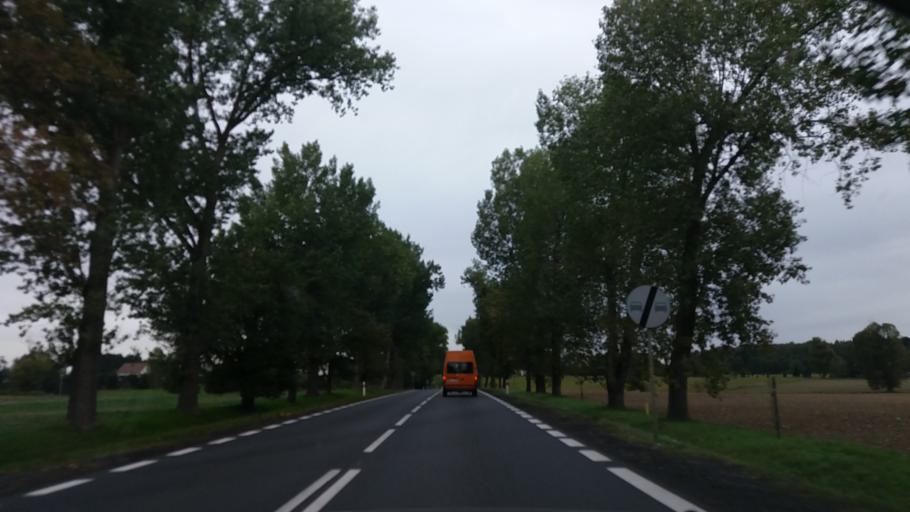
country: PL
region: Lower Silesian Voivodeship
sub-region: Powiat legnicki
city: Prochowice
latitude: 51.3111
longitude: 16.3286
